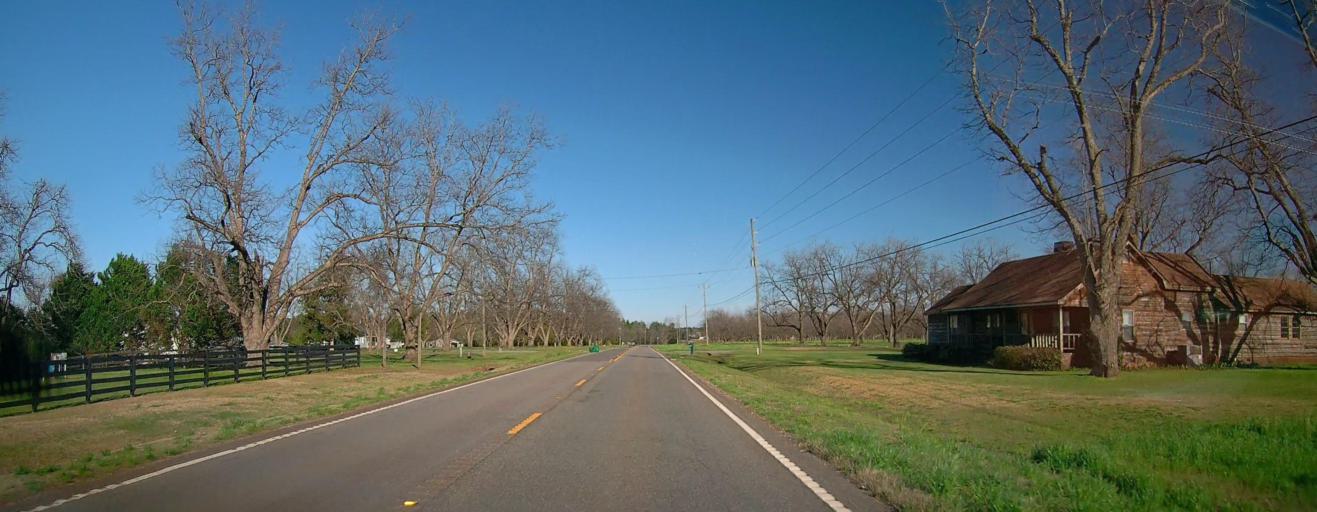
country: US
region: Georgia
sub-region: Houston County
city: Perry
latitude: 32.4409
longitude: -83.8044
